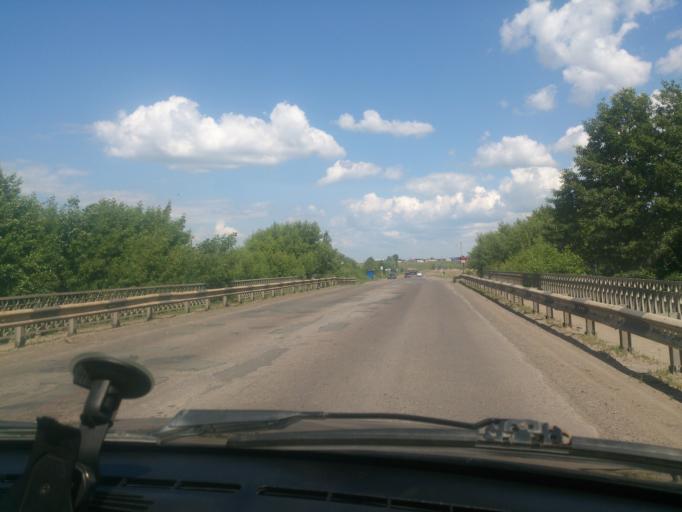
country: RU
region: Ulyanovsk
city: Cherdakly
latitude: 54.4325
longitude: 48.9006
